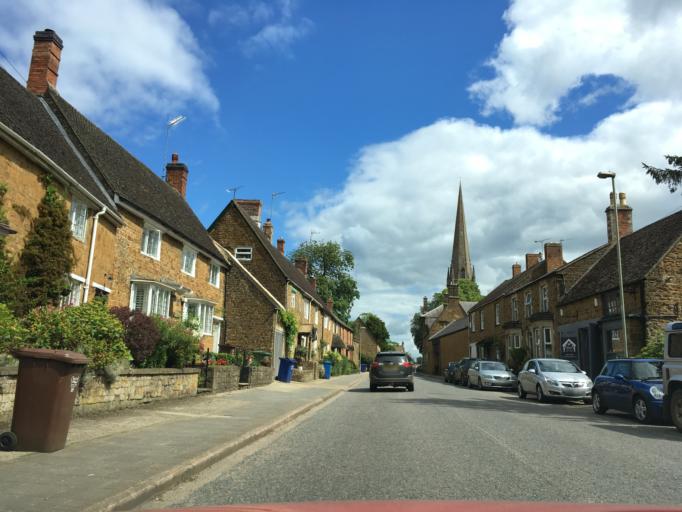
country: GB
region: England
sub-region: Oxfordshire
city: Bloxham
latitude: 52.0165
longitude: -1.3759
